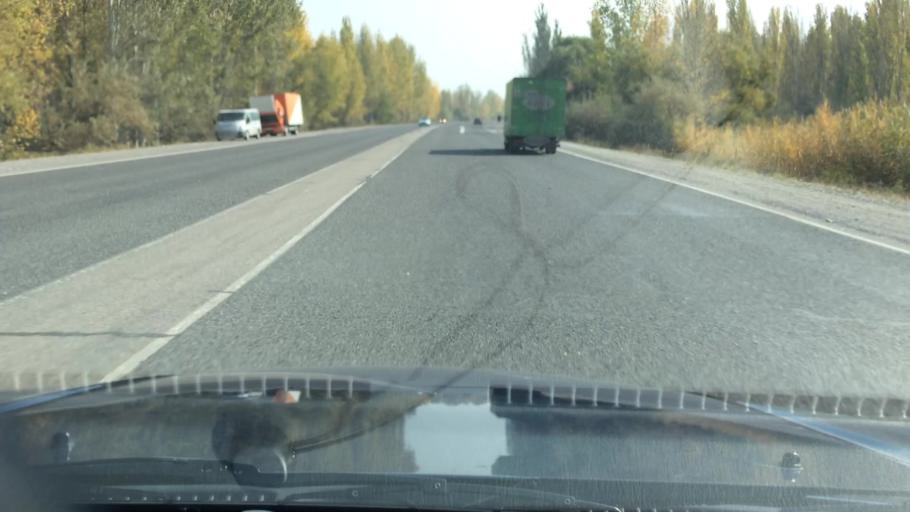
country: KG
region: Chuy
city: Ivanovka
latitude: 42.9386
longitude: 74.9821
